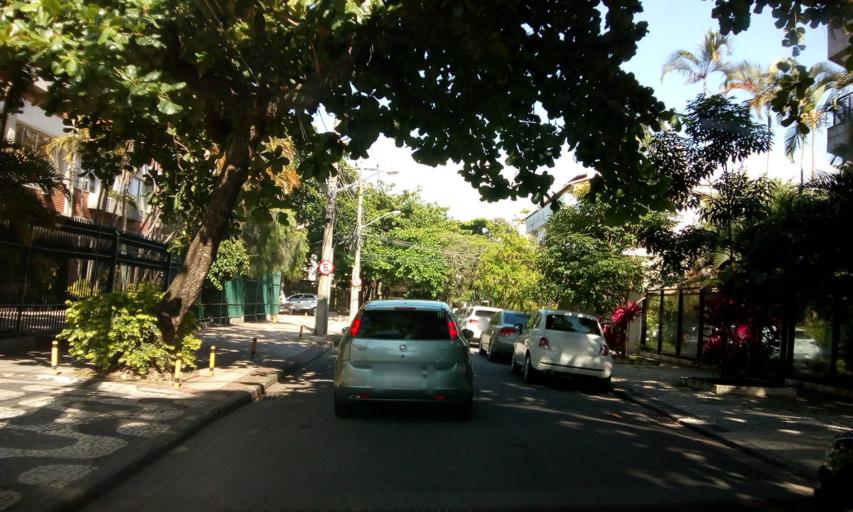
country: BR
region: Rio de Janeiro
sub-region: Rio De Janeiro
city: Rio de Janeiro
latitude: -23.0087
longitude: -43.3081
